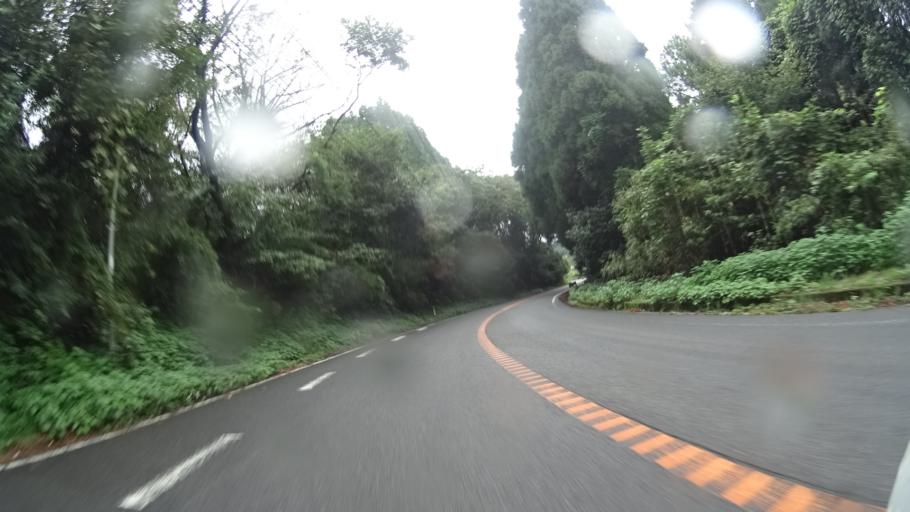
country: JP
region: Kagoshima
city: Kajiki
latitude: 31.7796
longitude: 130.6721
